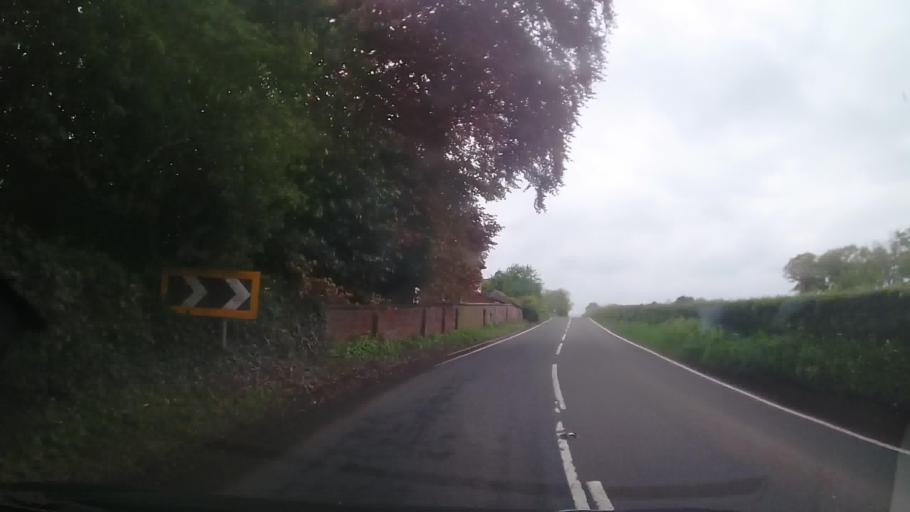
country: GB
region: Wales
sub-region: Wrexham
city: Overton
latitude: 52.9801
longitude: -2.9837
